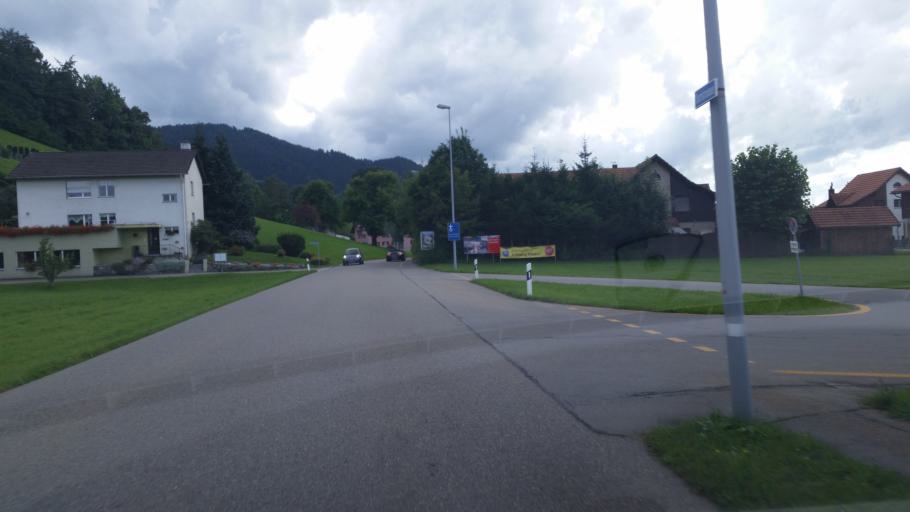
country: CH
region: Zurich
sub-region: Bezirk Horgen
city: Richterswil / Burghalde
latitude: 47.1774
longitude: 8.6721
